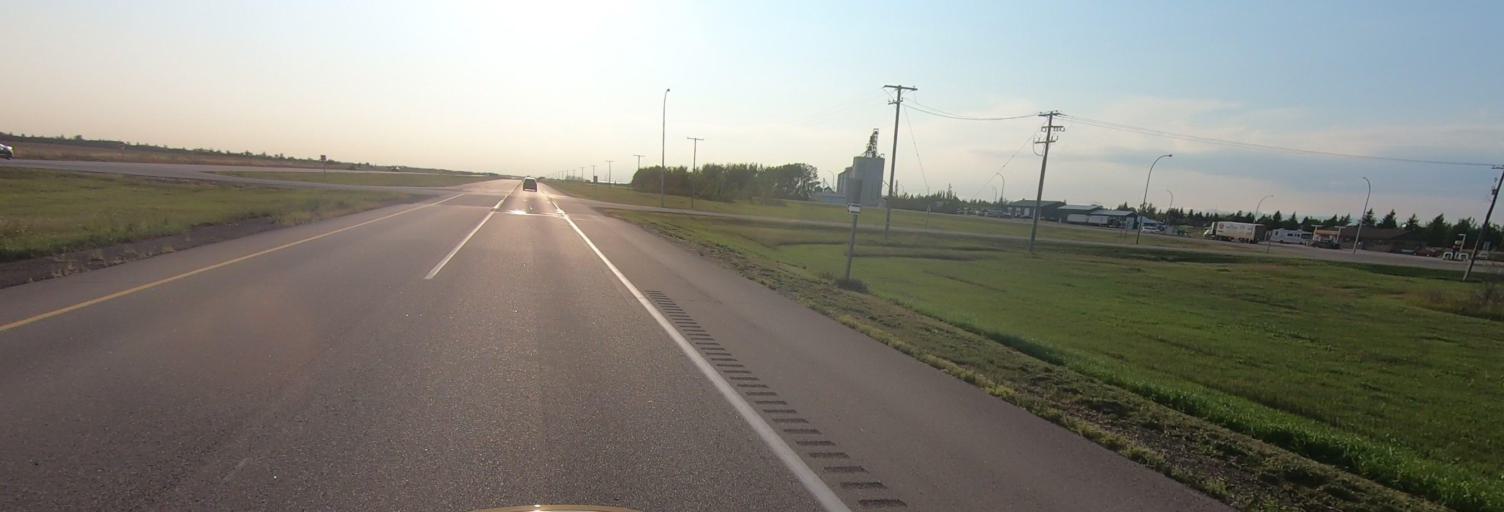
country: CA
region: Saskatchewan
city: Indian Head
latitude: 50.5259
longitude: -103.6546
